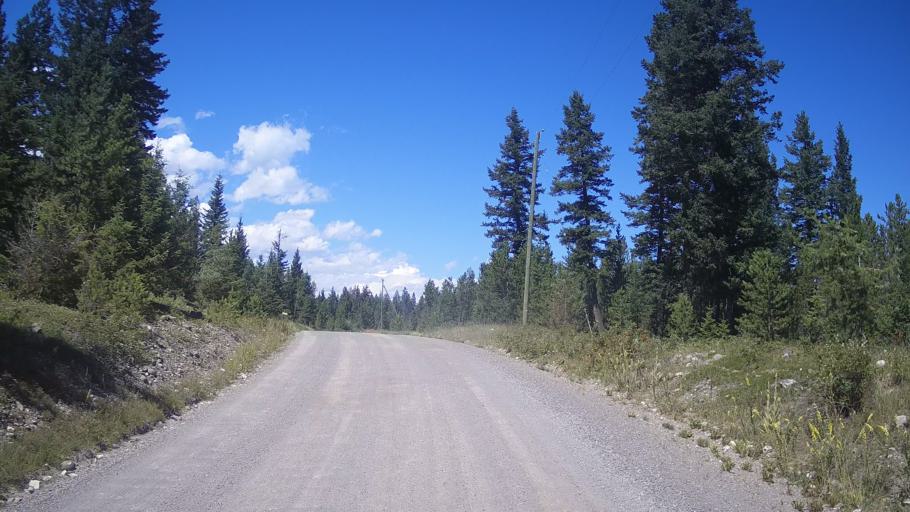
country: CA
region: British Columbia
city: Cache Creek
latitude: 51.2030
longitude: -121.5934
